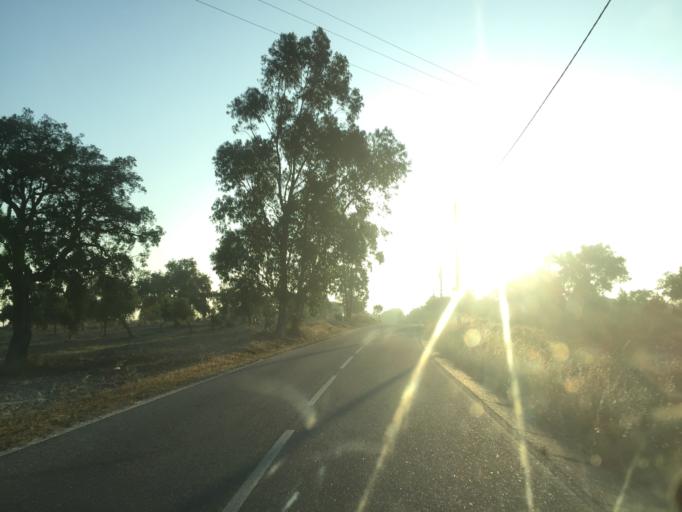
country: PT
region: Santarem
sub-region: Coruche
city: Coruche
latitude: 39.0593
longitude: -8.4139
